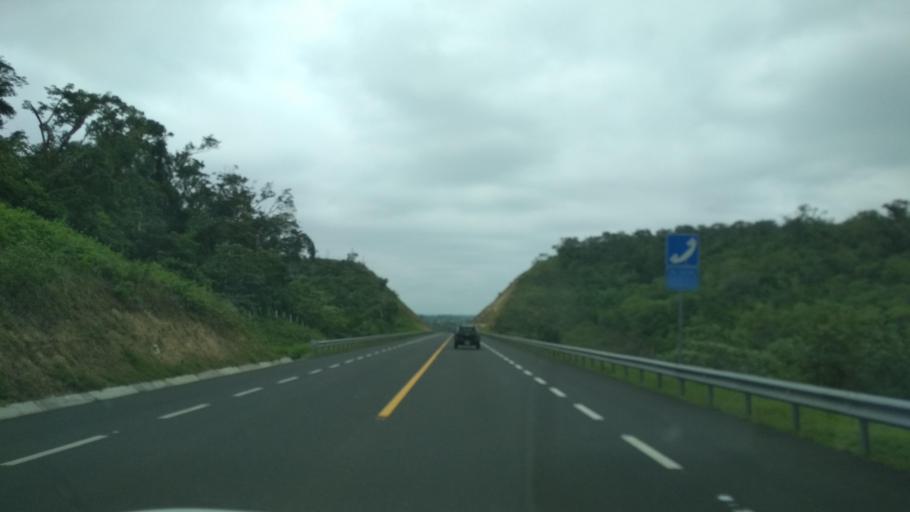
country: MX
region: Veracruz
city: Agua Dulce
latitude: 20.4215
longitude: -97.2176
